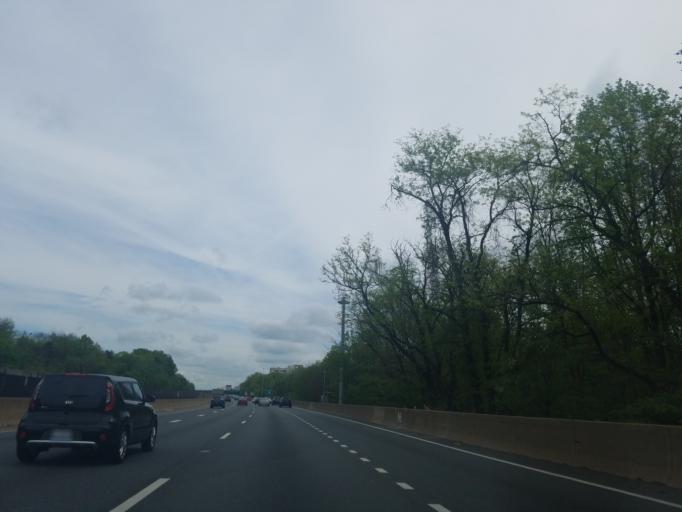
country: US
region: Virginia
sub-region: Fairfax County
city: Merrifield
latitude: 38.8803
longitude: -77.2377
